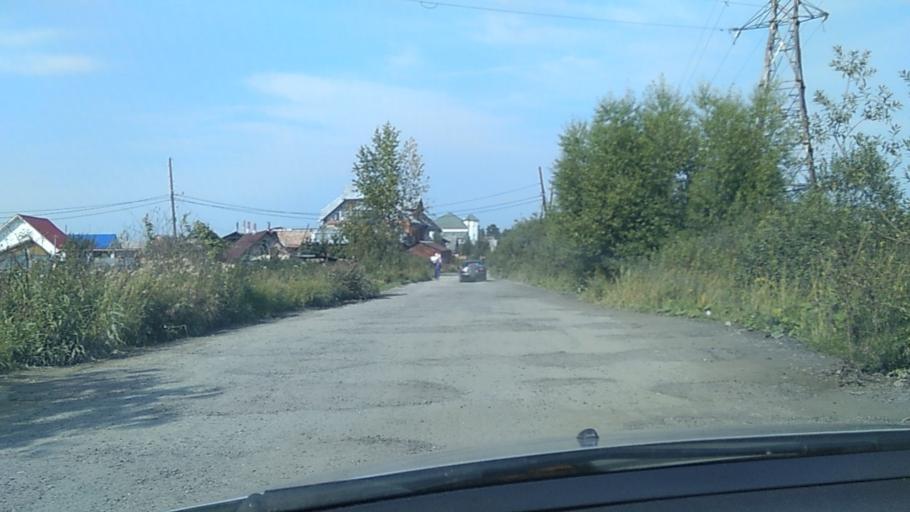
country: RU
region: Sverdlovsk
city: Sredneuralsk
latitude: 56.9751
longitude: 60.4745
